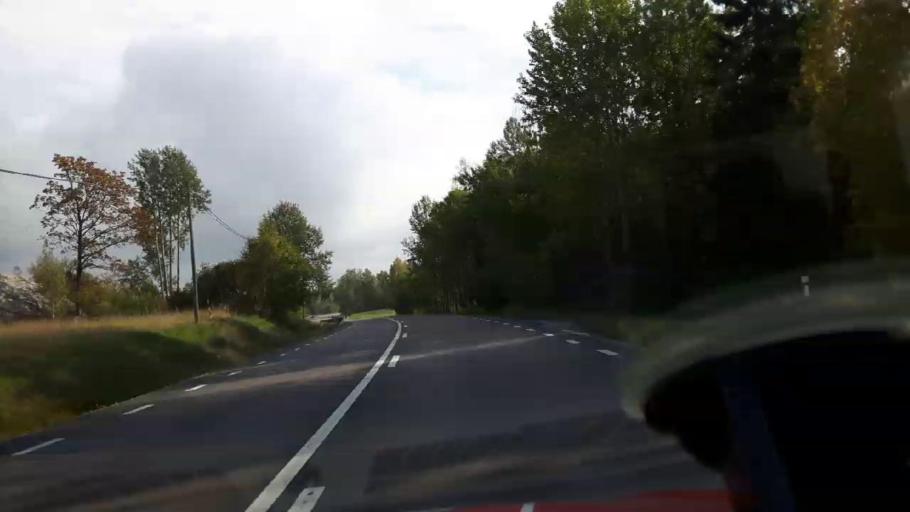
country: SE
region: Gaevleborg
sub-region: Bollnas Kommun
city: Kilafors
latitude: 61.1730
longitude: 16.7997
